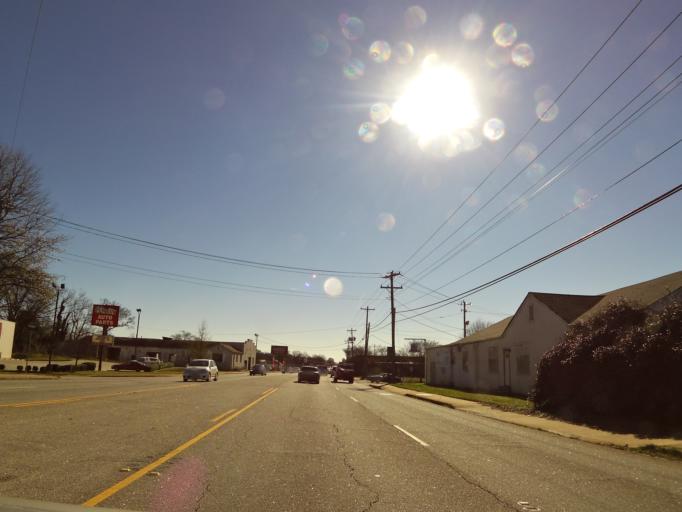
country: US
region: South Carolina
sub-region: Greenville County
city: Sans Souci
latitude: 34.8773
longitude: -82.4045
